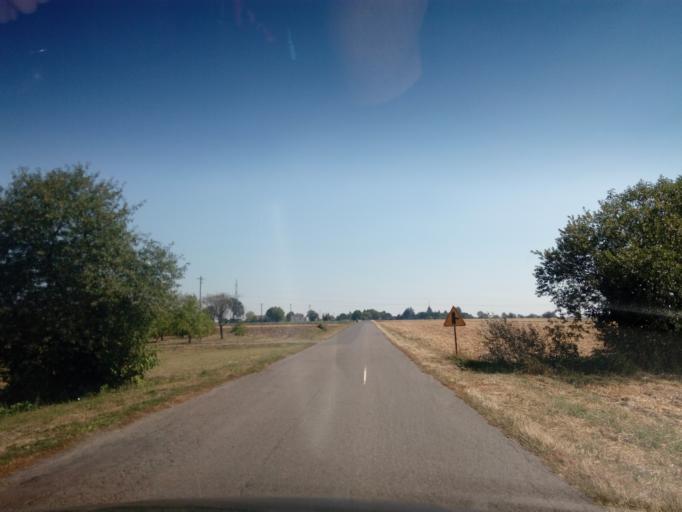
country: PL
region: Lublin Voivodeship
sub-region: Powiat hrubieszowski
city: Hrubieszow
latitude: 50.7298
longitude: 23.9119
